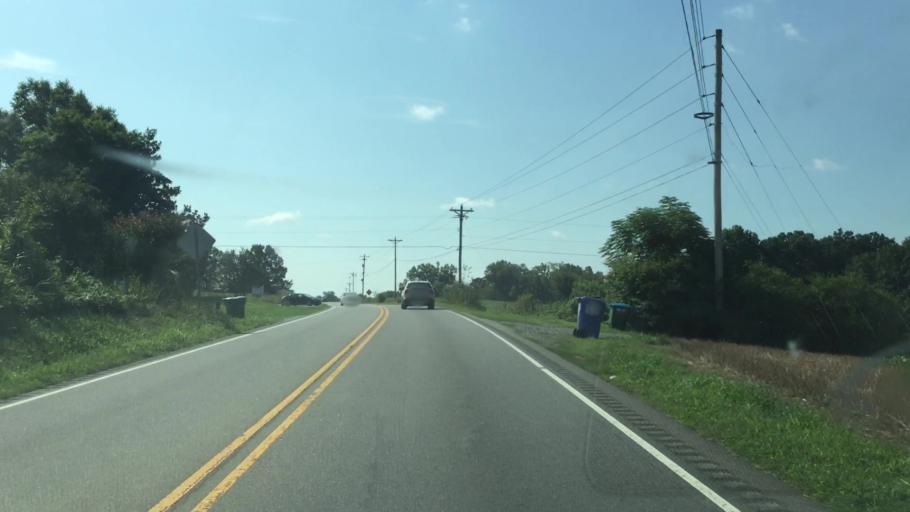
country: US
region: North Carolina
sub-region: Union County
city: Fairview
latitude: 35.1590
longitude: -80.5664
